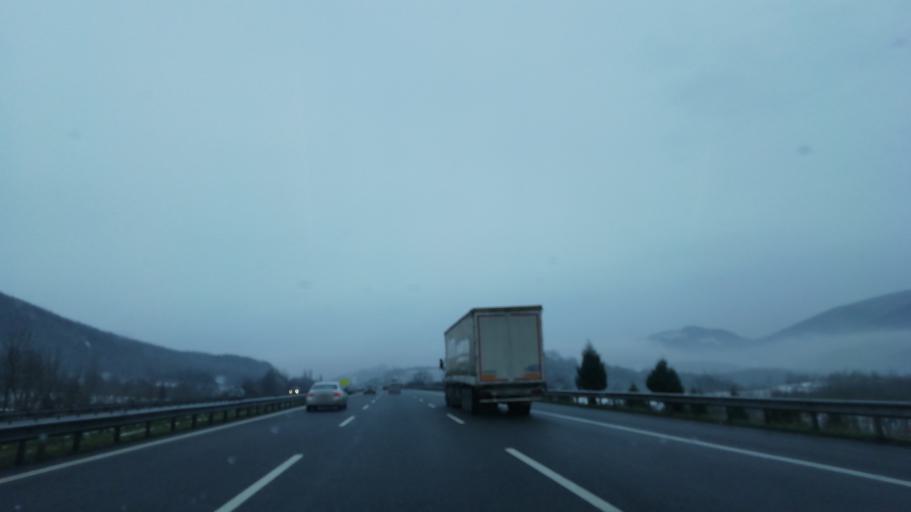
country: TR
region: Duzce
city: Gumusova
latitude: 40.8078
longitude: 30.8818
